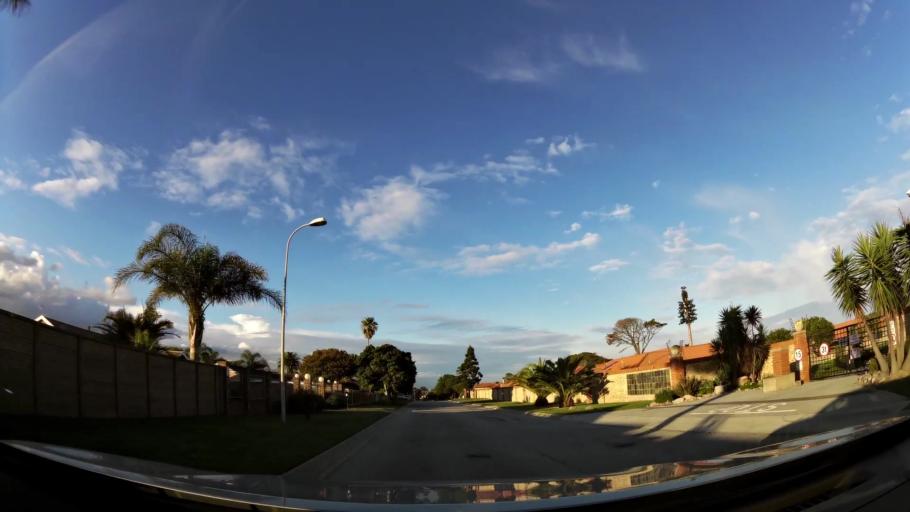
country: ZA
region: Eastern Cape
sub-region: Nelson Mandela Bay Metropolitan Municipality
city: Port Elizabeth
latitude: -33.9737
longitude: 25.4956
